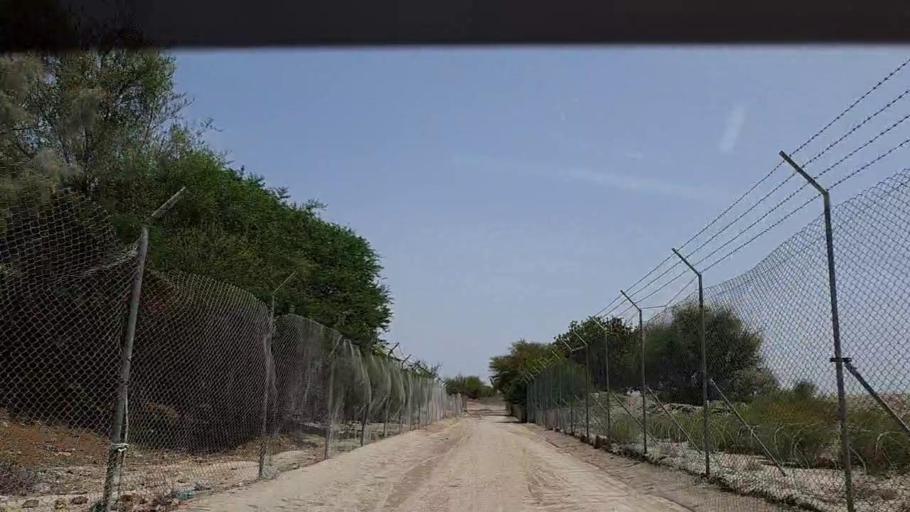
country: PK
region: Sindh
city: Johi
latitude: 26.7078
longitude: 67.6684
